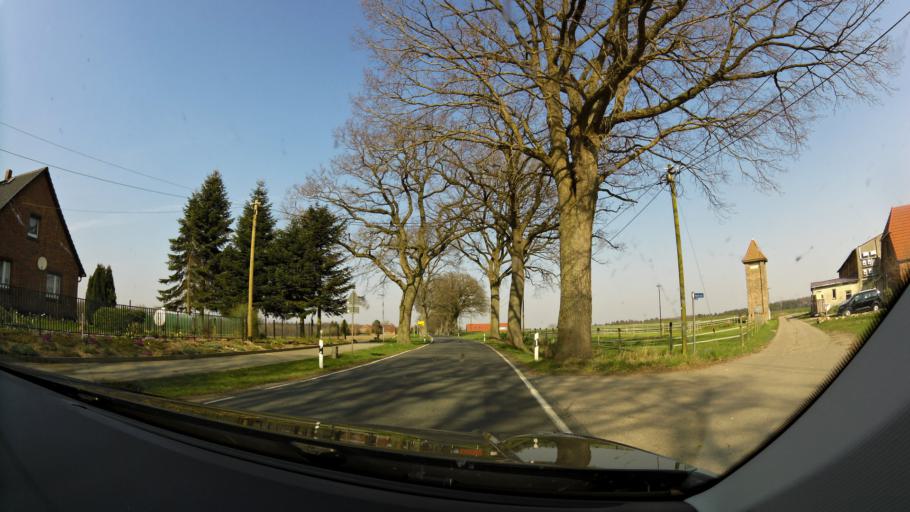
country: DE
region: Mecklenburg-Vorpommern
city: Marlow
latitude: 54.1270
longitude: 12.5306
